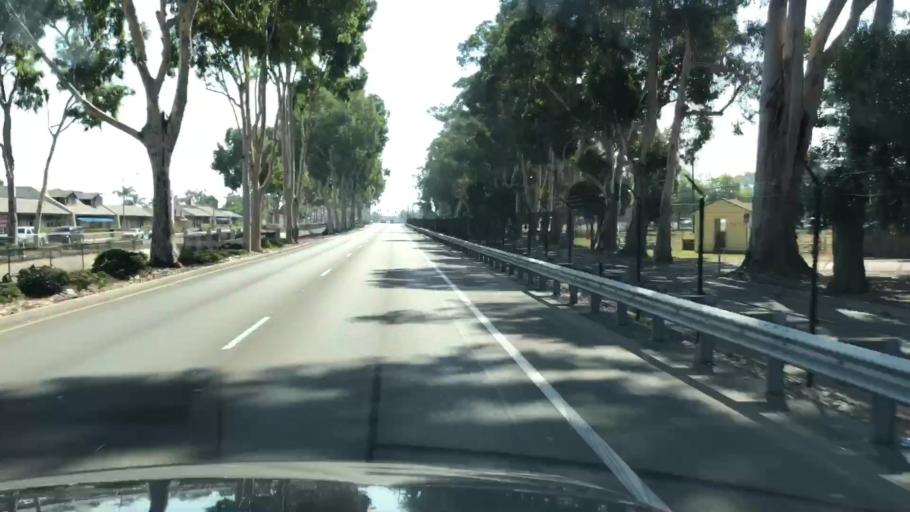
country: US
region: California
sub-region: Ventura County
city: Port Hueneme
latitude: 34.1757
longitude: -119.1993
